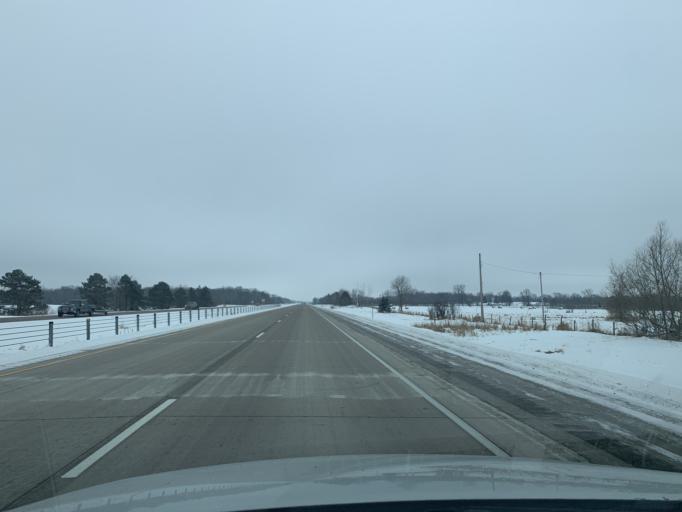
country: US
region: Minnesota
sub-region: Chisago County
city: Rush City
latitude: 45.6451
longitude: -92.9925
